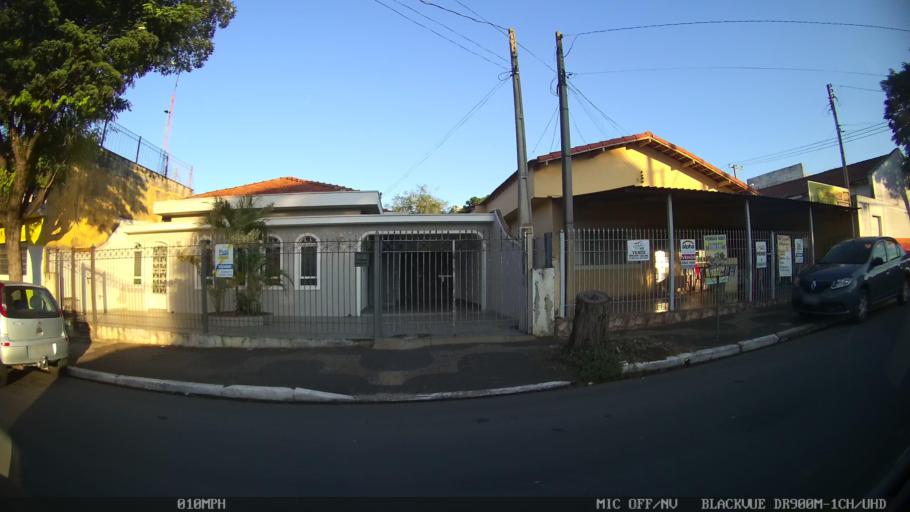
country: BR
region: Sao Paulo
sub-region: Sumare
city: Sumare
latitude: -22.8065
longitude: -47.2214
